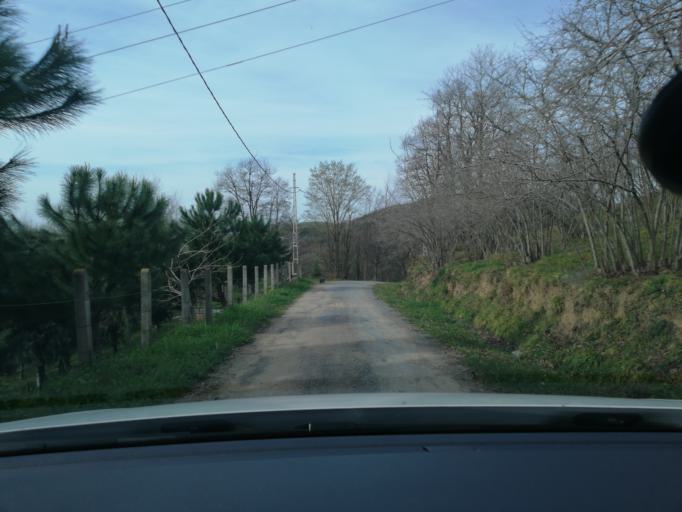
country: TR
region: Zonguldak
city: Kozlu
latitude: 41.3582
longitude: 31.6239
